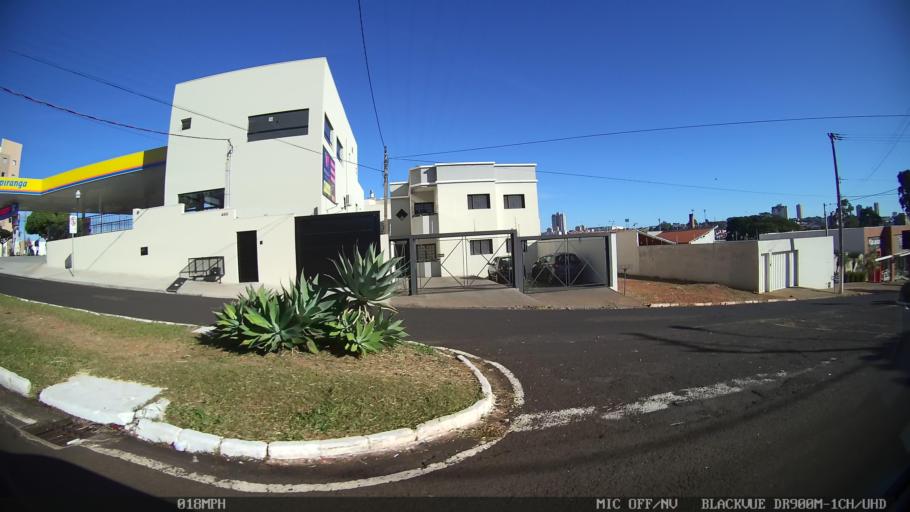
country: BR
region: Sao Paulo
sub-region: Franca
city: Franca
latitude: -20.5546
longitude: -47.4074
